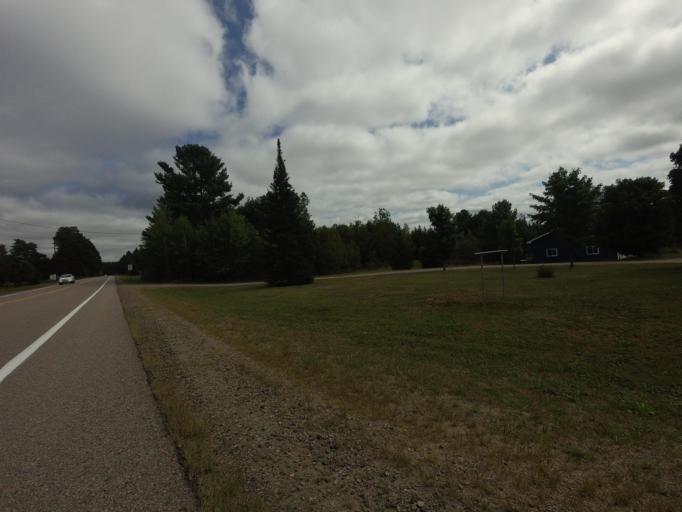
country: CA
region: Ontario
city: Bancroft
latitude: 44.9057
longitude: -78.4193
